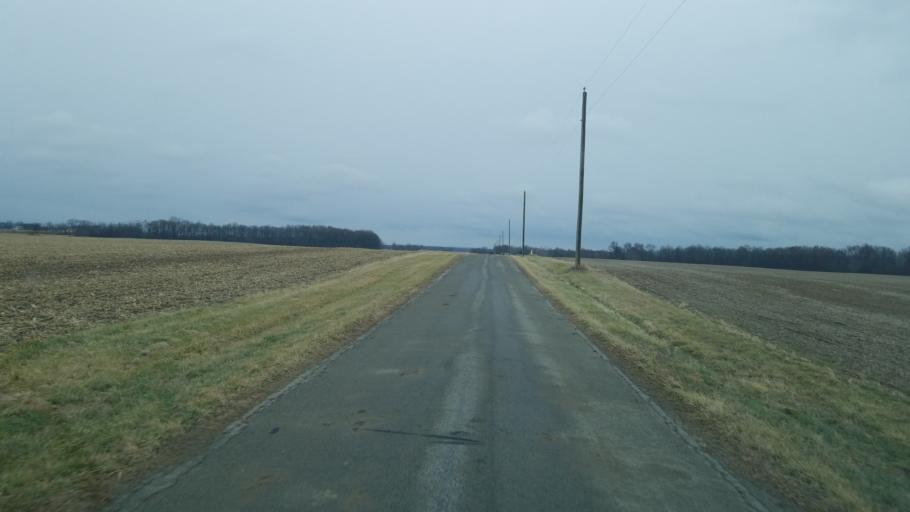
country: US
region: Ohio
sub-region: Union County
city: Marysville
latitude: 40.3089
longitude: -83.3121
